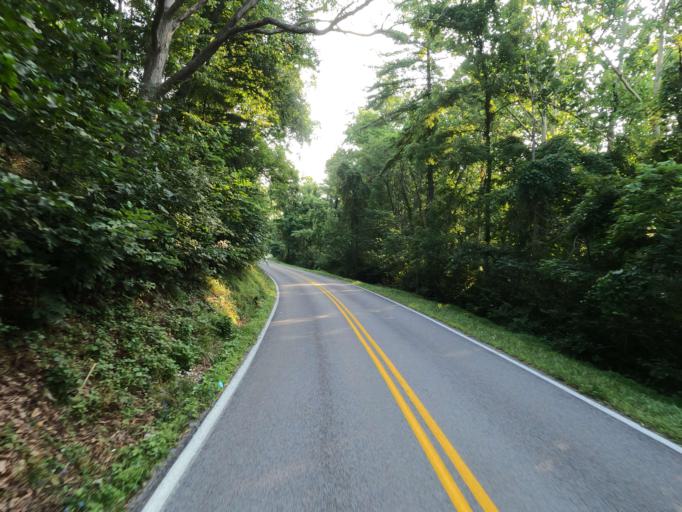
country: US
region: West Virginia
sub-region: Morgan County
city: Berkeley Springs
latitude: 39.6757
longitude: -78.2621
